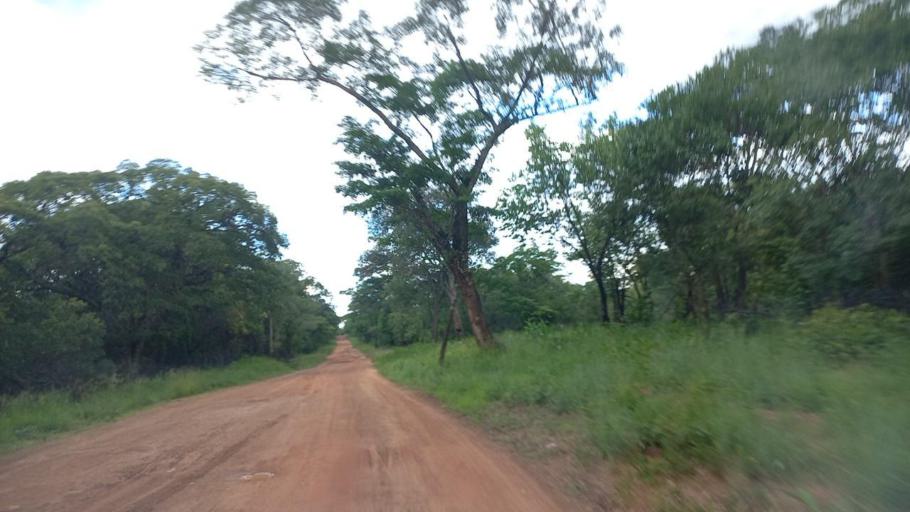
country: ZM
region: North-Western
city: Mwinilunga
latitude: -11.8355
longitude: 24.3681
